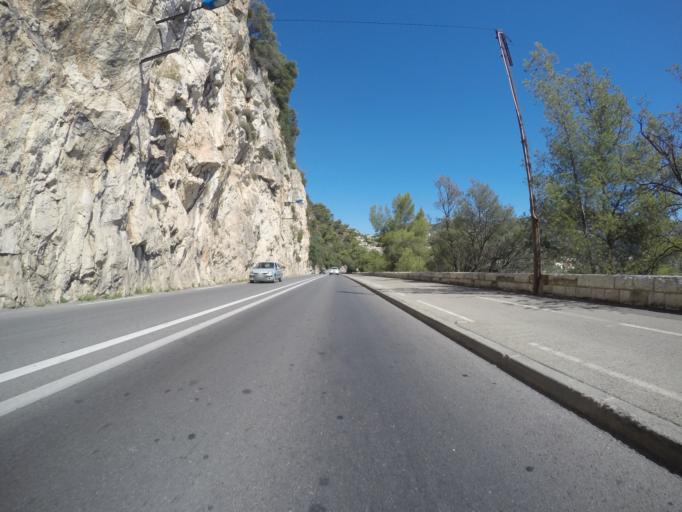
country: FR
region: Provence-Alpes-Cote d'Azur
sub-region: Departement des Alpes-Maritimes
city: Villefranche-sur-Mer
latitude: 43.6948
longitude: 7.3054
